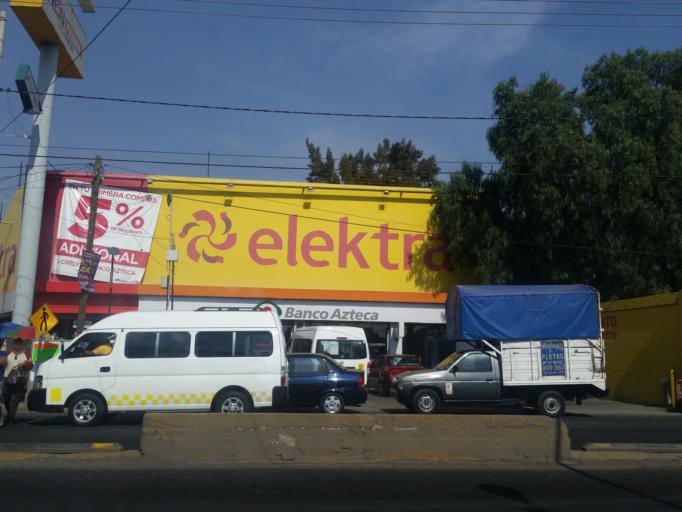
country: MX
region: Mexico
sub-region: La Paz
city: San Isidro
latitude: 19.3272
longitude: -98.9467
